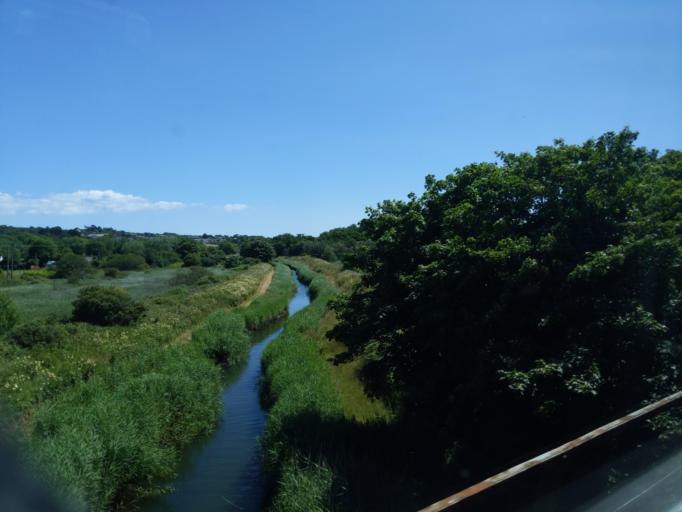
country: GB
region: England
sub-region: Cornwall
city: Hayle
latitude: 50.1740
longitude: -5.4338
